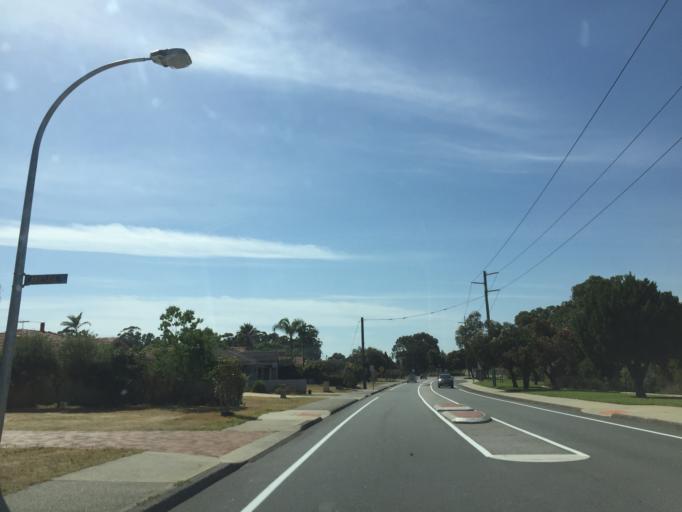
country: AU
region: Western Australia
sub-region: Gosnells
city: Thornlie
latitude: -32.0737
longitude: 115.9595
